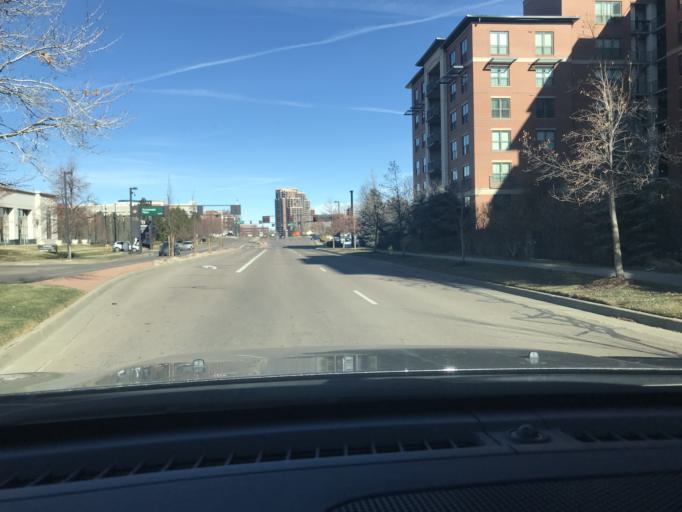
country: US
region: Colorado
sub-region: Arapahoe County
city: Castlewood
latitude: 39.6217
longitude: -104.8947
